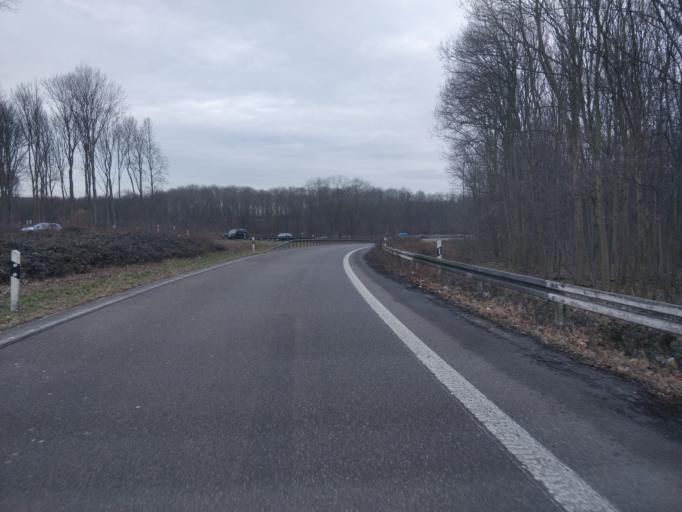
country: DE
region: North Rhine-Westphalia
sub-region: Regierungsbezirk Koln
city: Mengenich
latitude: 50.9959
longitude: 6.8936
